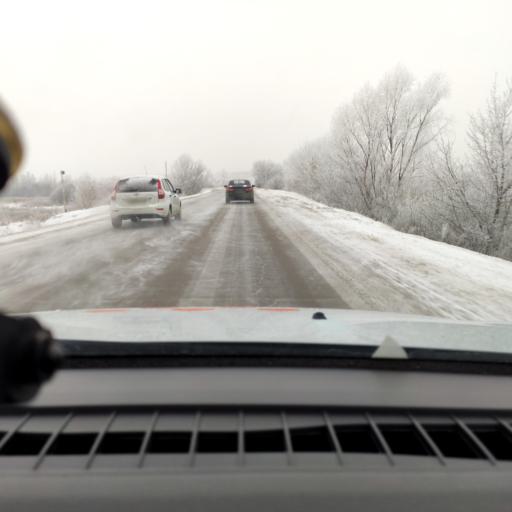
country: RU
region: Samara
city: Samara
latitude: 53.1055
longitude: 50.2269
